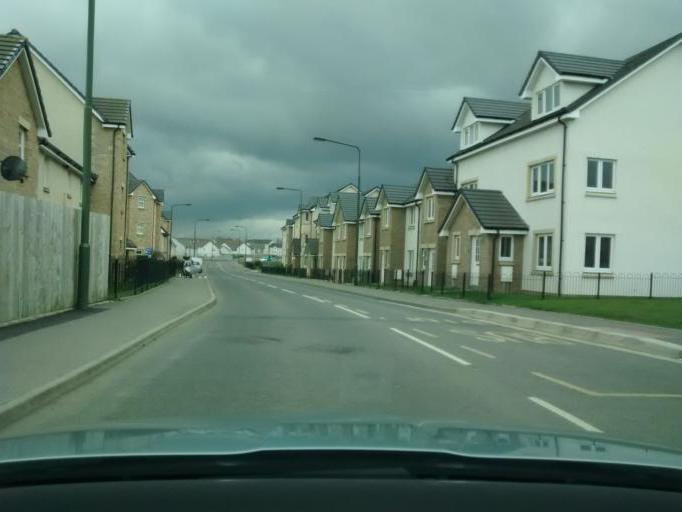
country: GB
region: Scotland
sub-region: West Lothian
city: Bathgate
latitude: 55.8900
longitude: -3.6463
